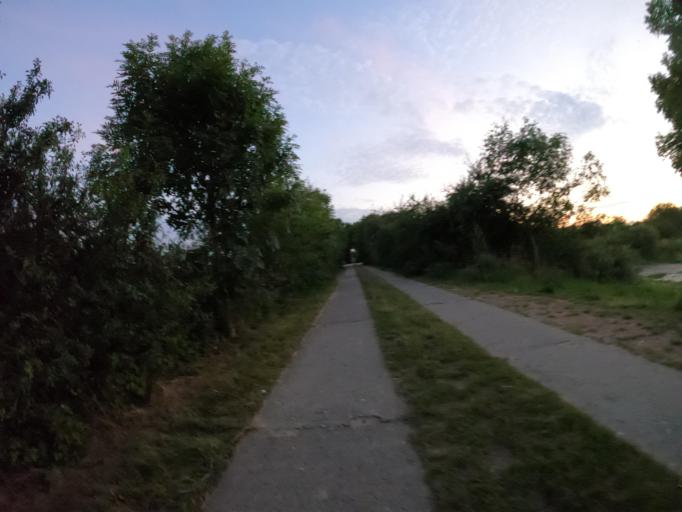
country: DE
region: Mecklenburg-Vorpommern
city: Woldegk
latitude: 53.4565
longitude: 13.5684
